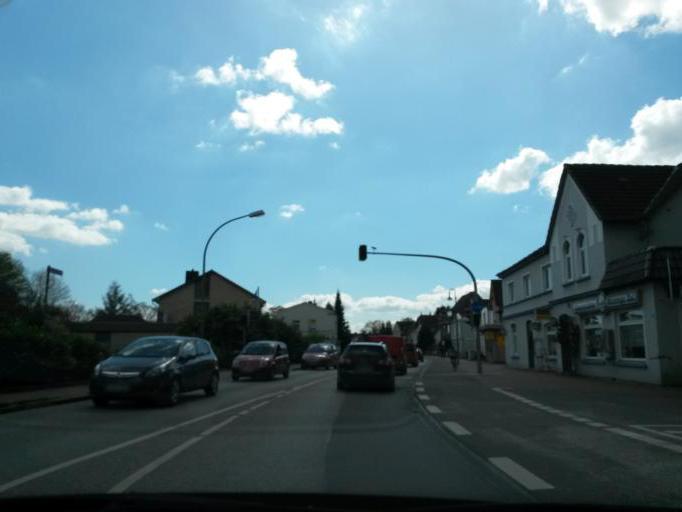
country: DE
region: Schleswig-Holstein
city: Moorrege
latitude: 53.6761
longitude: 9.6771
